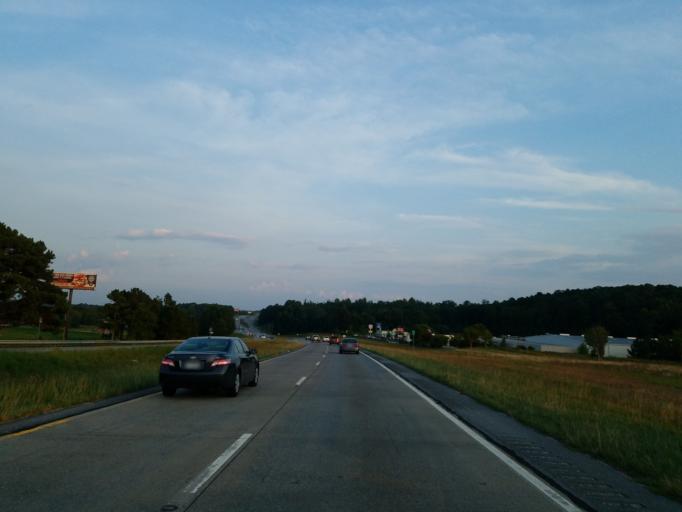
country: US
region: Georgia
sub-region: Pickens County
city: Jasper
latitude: 34.4781
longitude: -84.4667
